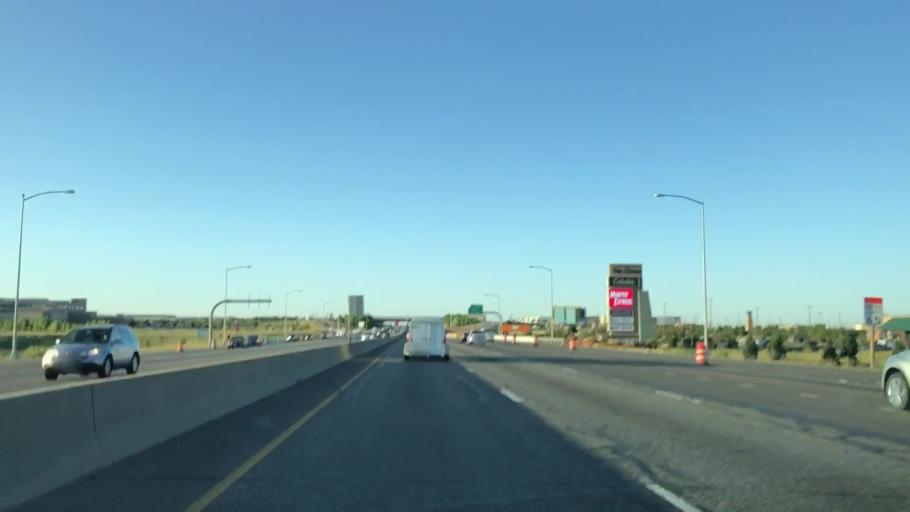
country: US
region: Colorado
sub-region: Adams County
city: Northglenn
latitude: 39.9494
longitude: -104.9874
